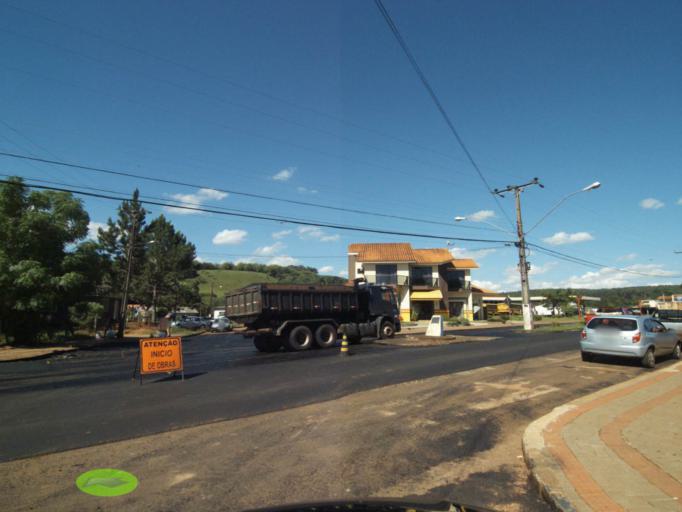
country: BR
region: Parana
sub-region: Coronel Vivida
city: Coronel Vivida
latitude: -26.1431
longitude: -52.3833
